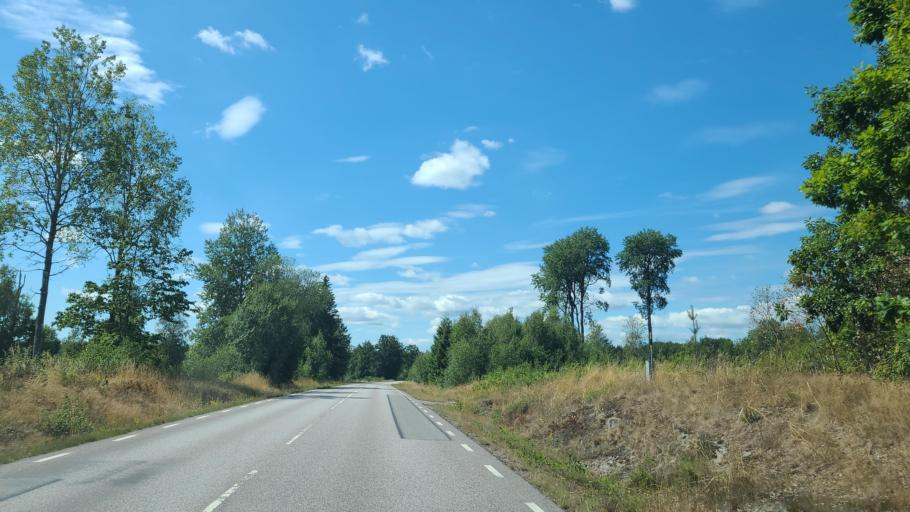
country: SE
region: Kalmar
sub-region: Emmaboda Kommun
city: Emmaboda
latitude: 56.5369
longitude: 15.6615
